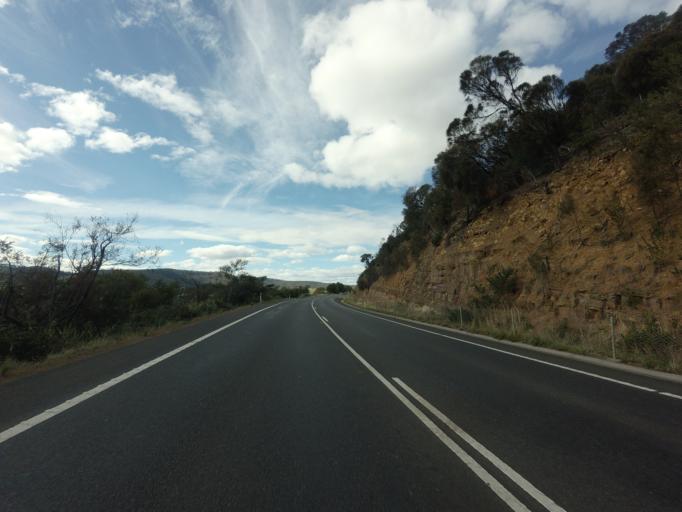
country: AU
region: Tasmania
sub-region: Glenorchy
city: Granton
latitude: -42.7477
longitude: 147.1771
